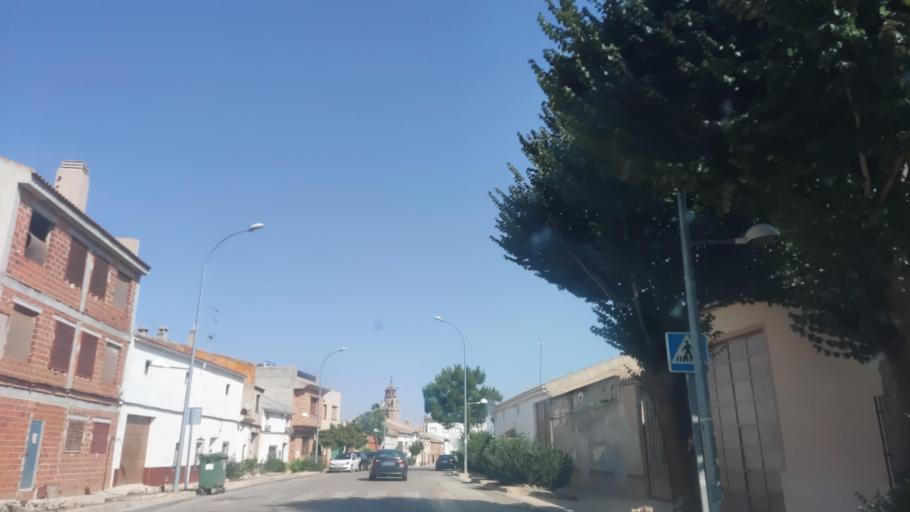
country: ES
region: Castille-La Mancha
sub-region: Provincia de Albacete
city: La Gineta
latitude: 39.1115
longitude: -1.9948
